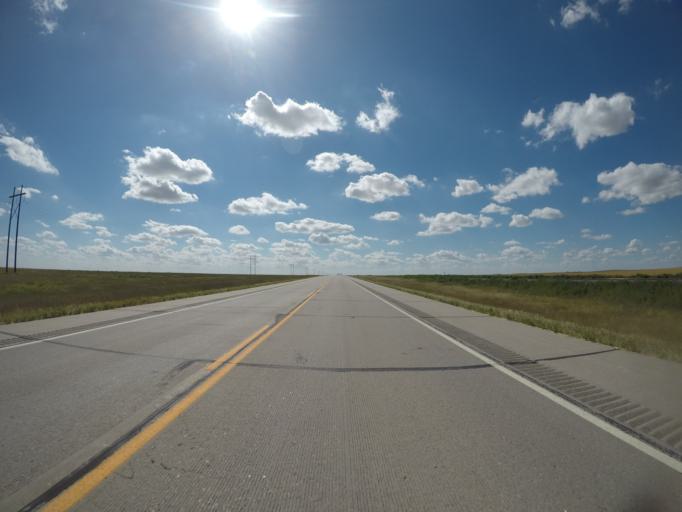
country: US
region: Colorado
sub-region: Phillips County
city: Holyoke
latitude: 40.6008
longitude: -102.4022
